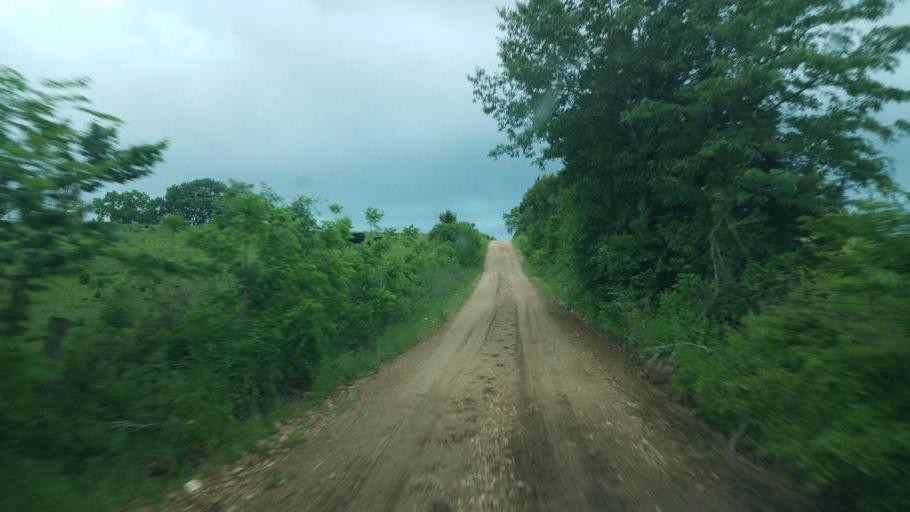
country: US
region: Missouri
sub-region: Moniteau County
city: California
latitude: 38.7503
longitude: -92.6240
